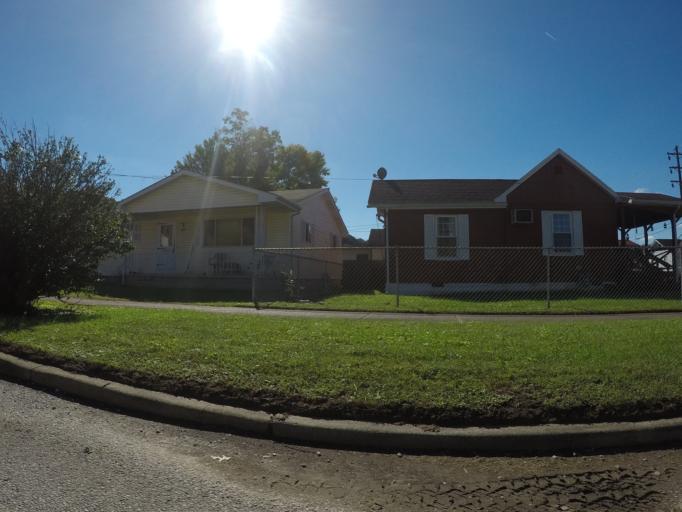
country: US
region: Ohio
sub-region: Lawrence County
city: Burlington
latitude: 38.3981
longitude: -82.5196
